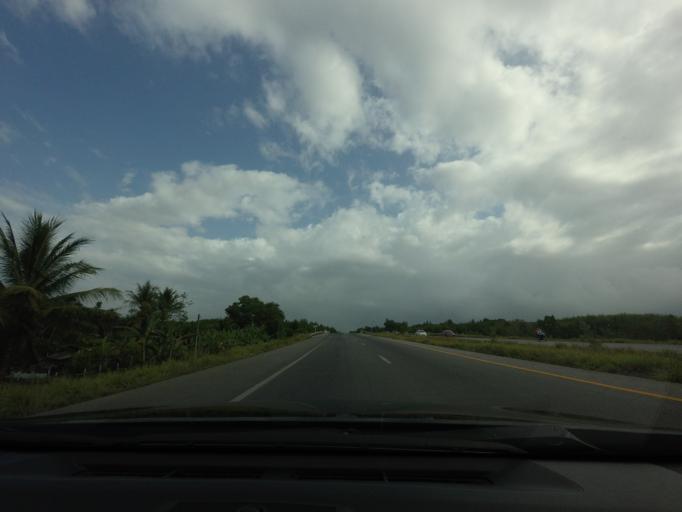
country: TH
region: Pattani
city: Mae Lan
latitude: 6.6691
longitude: 101.2342
